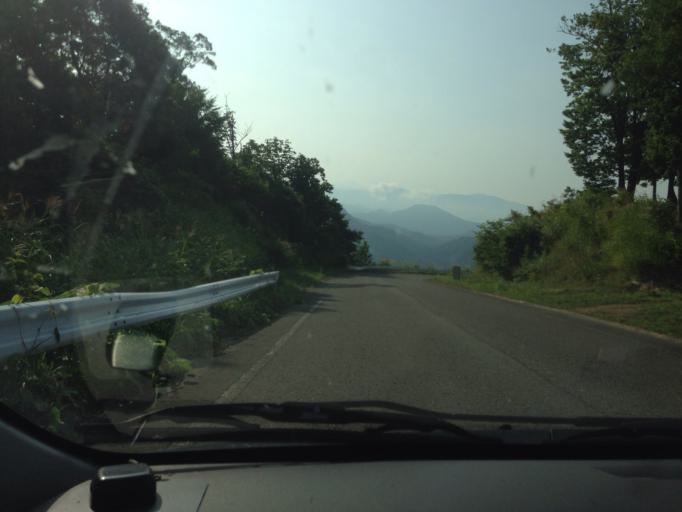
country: JP
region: Fukushima
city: Kitakata
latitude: 37.7478
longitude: 139.8682
